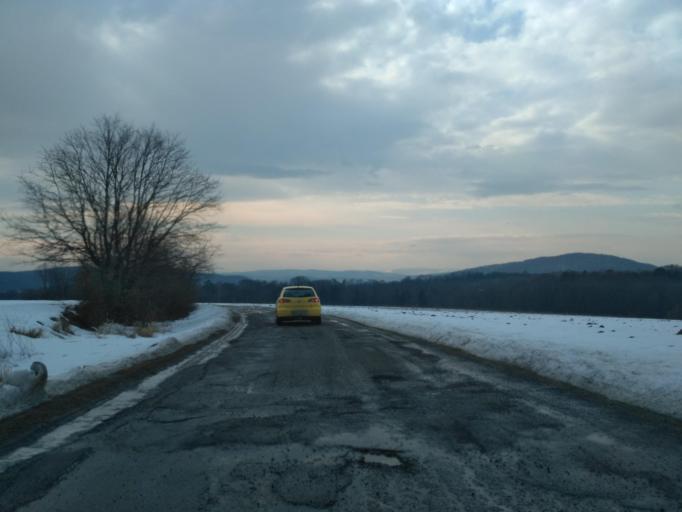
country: PL
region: Subcarpathian Voivodeship
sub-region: Powiat brzozowski
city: Dydnia
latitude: 49.6467
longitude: 22.1599
